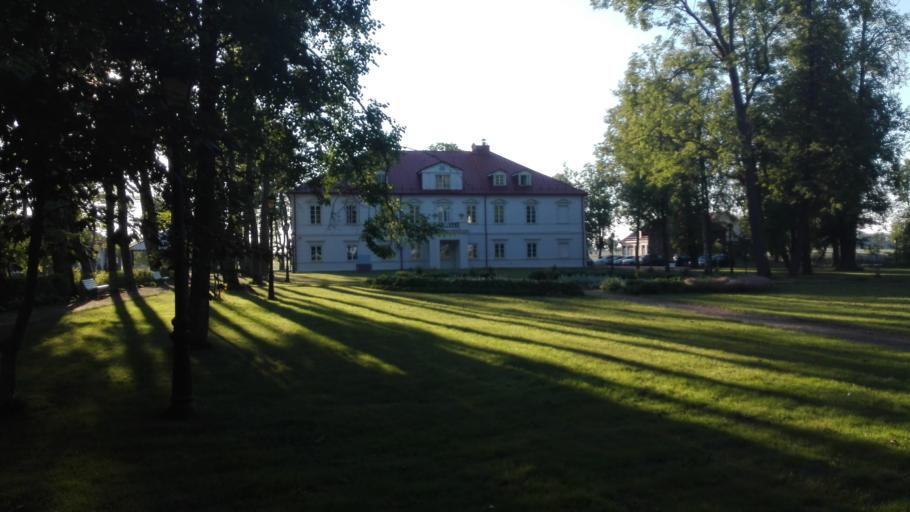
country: LT
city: Ramygala
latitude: 55.5963
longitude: 24.3572
